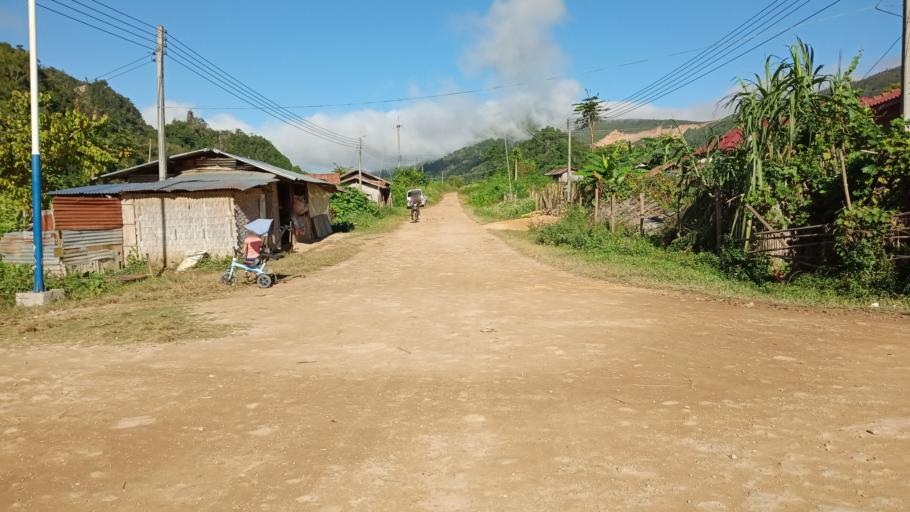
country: LA
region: Xiangkhoang
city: Phonsavan
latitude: 19.1133
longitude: 102.9144
